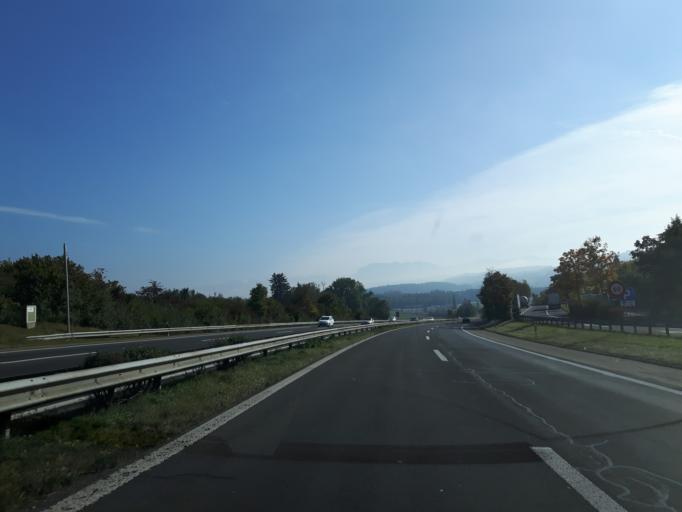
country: CH
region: Lucerne
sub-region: Sursee District
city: Knutwil
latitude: 47.1908
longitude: 8.0762
